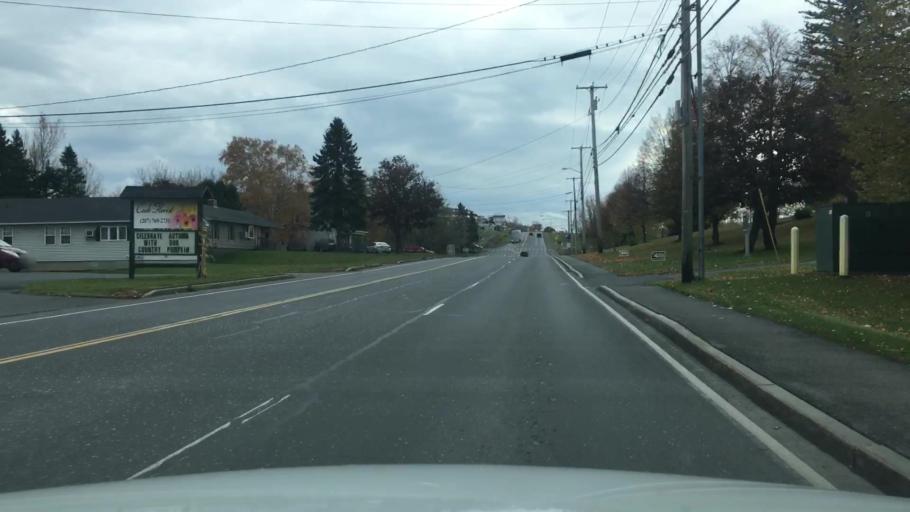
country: US
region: Maine
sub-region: Aroostook County
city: Presque Isle
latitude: 46.6722
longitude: -68.0150
